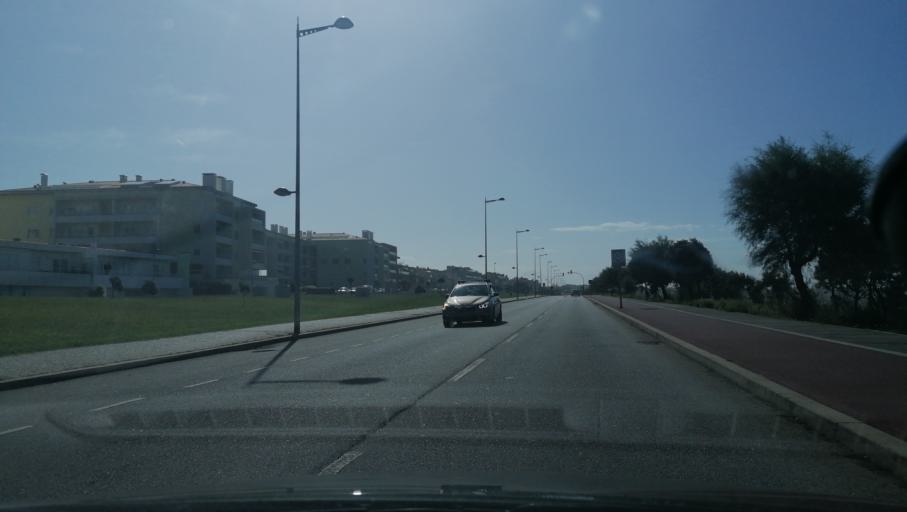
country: PT
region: Aveiro
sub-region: Espinho
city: Espinho
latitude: 41.0237
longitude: -8.6425
